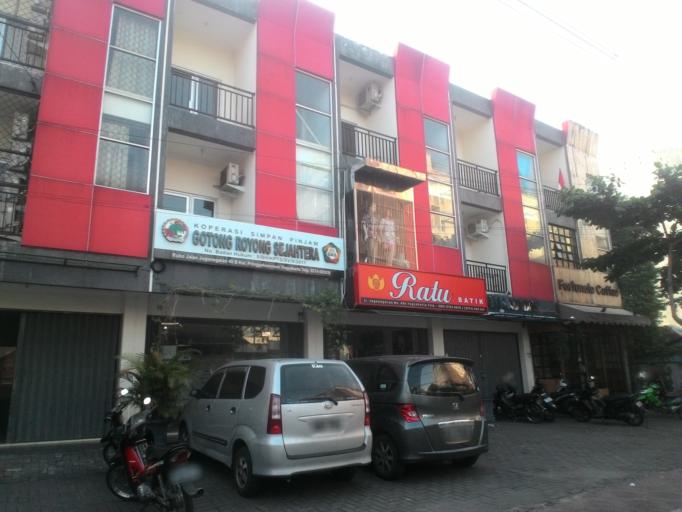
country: ID
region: Daerah Istimewa Yogyakarta
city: Yogyakarta
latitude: -7.7942
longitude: 110.3613
